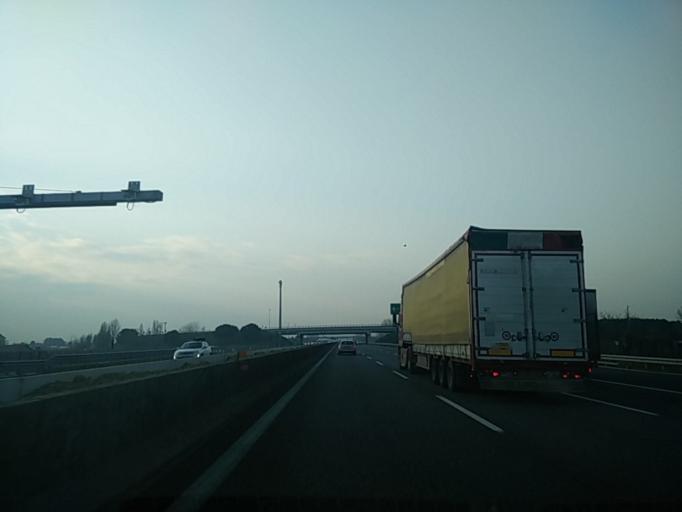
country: IT
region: Emilia-Romagna
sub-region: Provincia di Ravenna
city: Solarolo
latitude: 44.3530
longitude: 11.8190
